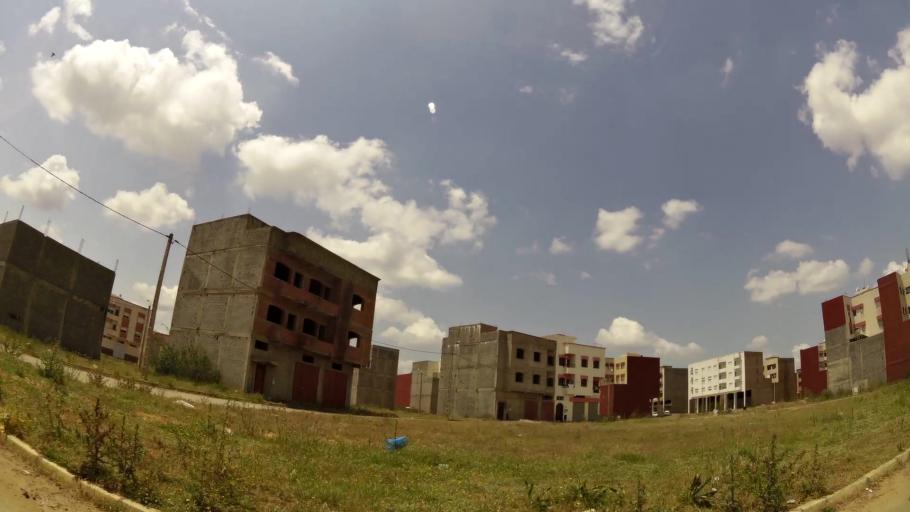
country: MA
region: Rabat-Sale-Zemmour-Zaer
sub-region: Khemisset
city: Tiflet
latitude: 34.0092
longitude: -6.5222
